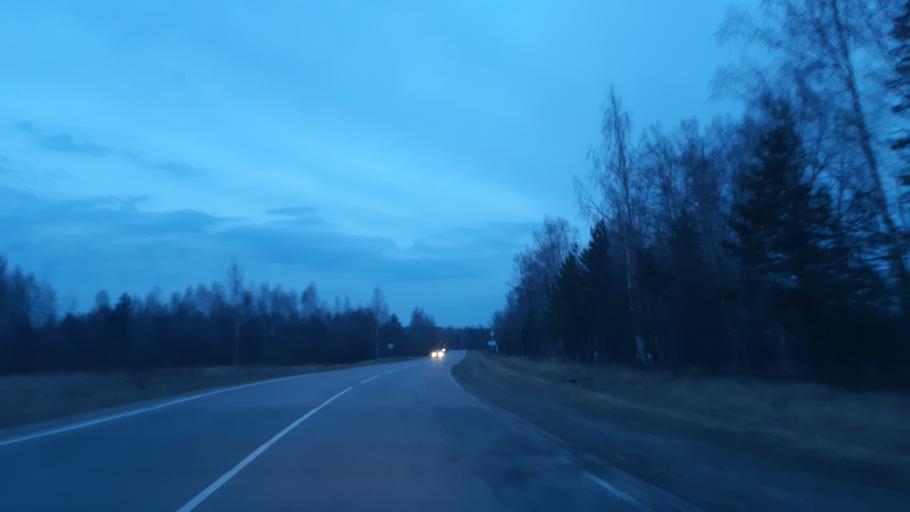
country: RU
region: Vladimir
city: Nikologory
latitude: 56.1750
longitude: 42.0038
